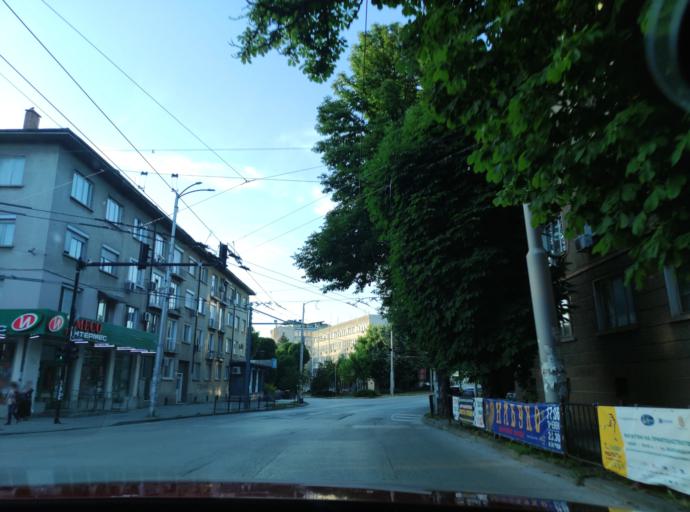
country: BG
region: Pleven
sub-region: Obshtina Pleven
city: Pleven
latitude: 43.4049
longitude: 24.6209
